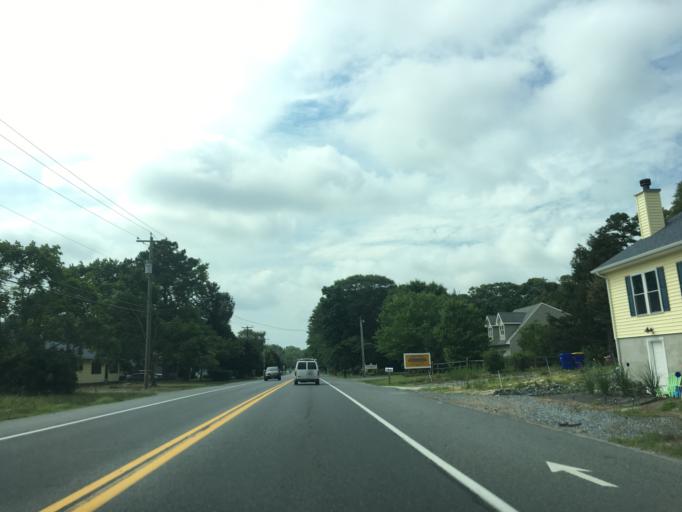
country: US
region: Delaware
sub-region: Sussex County
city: Ocean View
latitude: 38.5518
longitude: -75.1507
